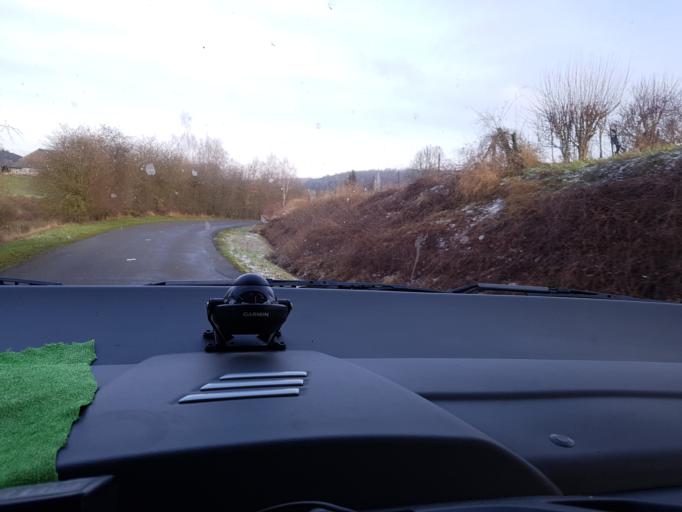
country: FR
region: Champagne-Ardenne
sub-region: Departement des Ardennes
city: Tournes
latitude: 49.7438
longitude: 4.6003
